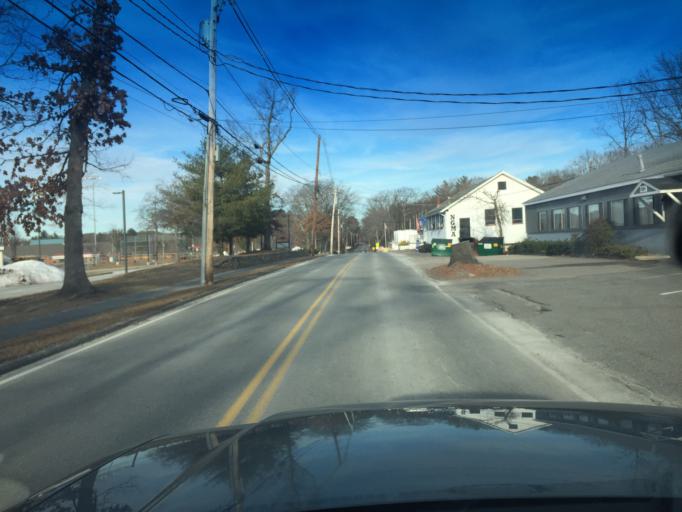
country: US
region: Massachusetts
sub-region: Middlesex County
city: Holliston
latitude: 42.2039
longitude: -71.4224
